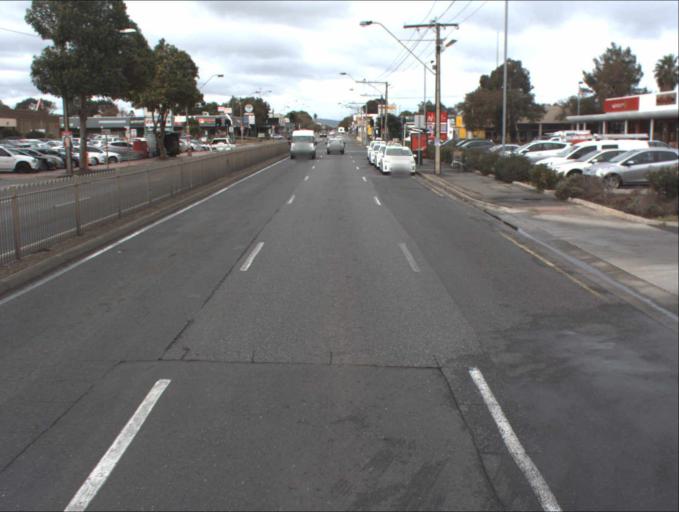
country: AU
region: South Australia
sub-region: Prospect
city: Prospect
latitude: -34.8759
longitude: 138.6021
